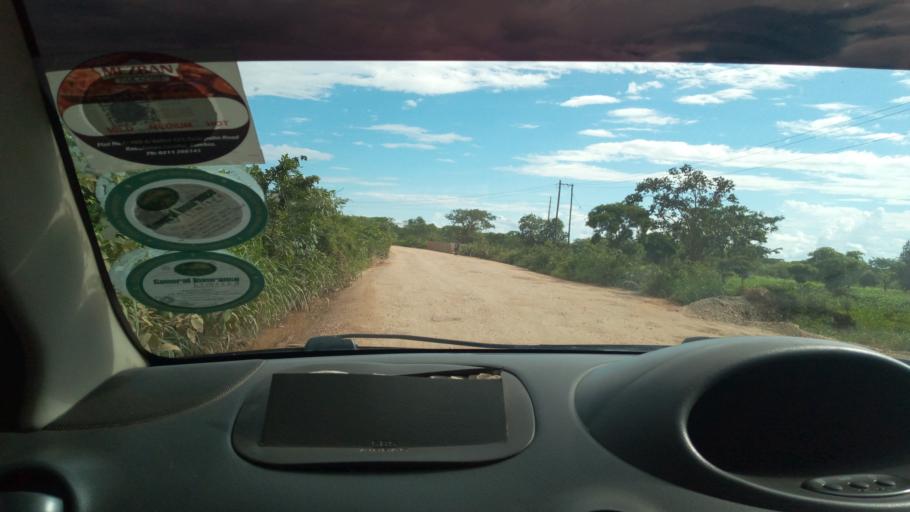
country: ZM
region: Lusaka
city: Lusaka
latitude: -15.5318
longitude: 28.3429
